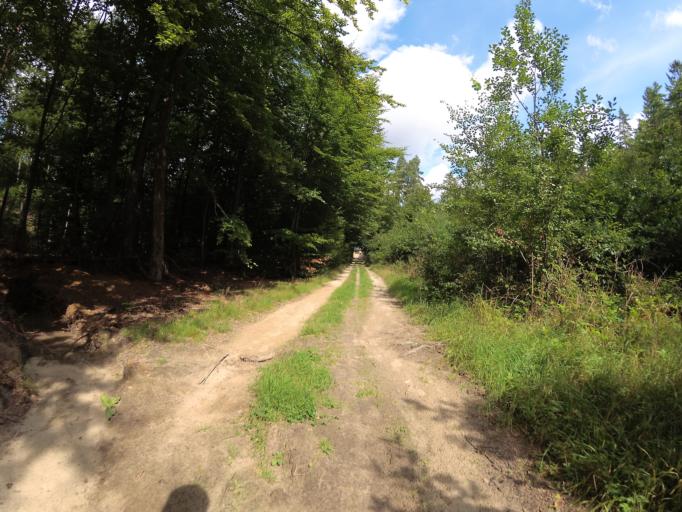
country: PL
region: Pomeranian Voivodeship
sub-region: Gdynia
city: Wielki Kack
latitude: 54.5117
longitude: 18.4788
